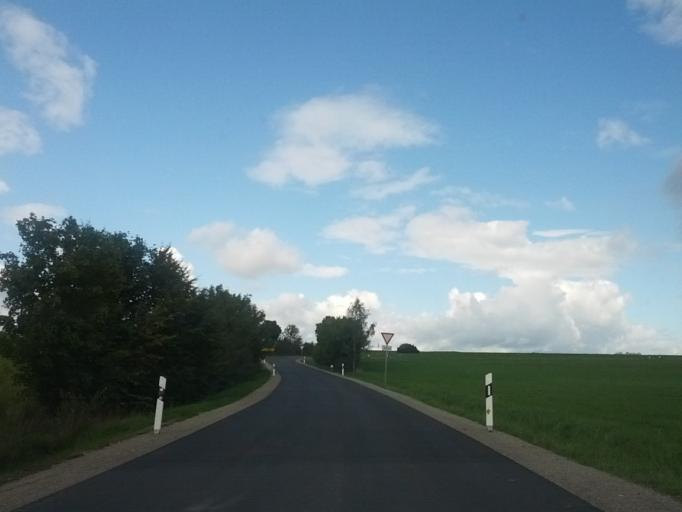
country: DE
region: Hesse
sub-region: Regierungsbezirk Kassel
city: Weissenborn
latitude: 51.0848
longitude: 10.0623
